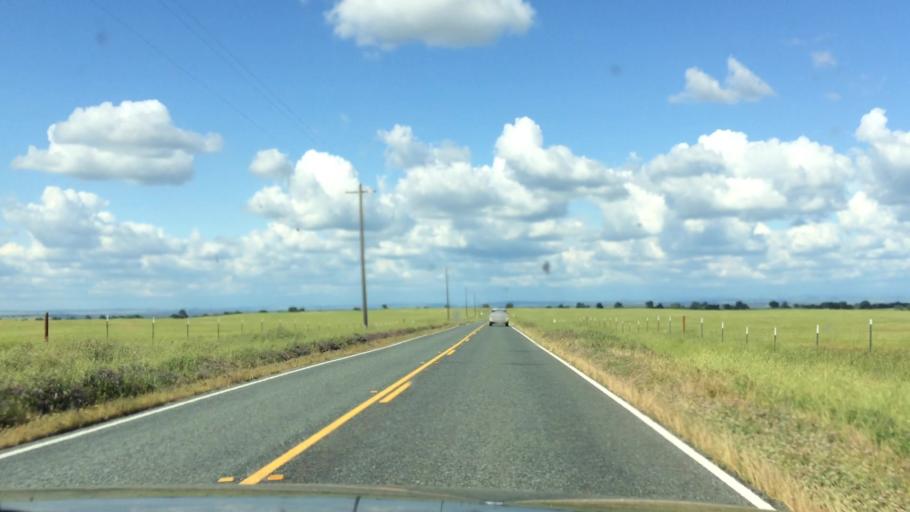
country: US
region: California
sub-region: Sacramento County
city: Clay
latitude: 38.3732
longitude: -121.0671
